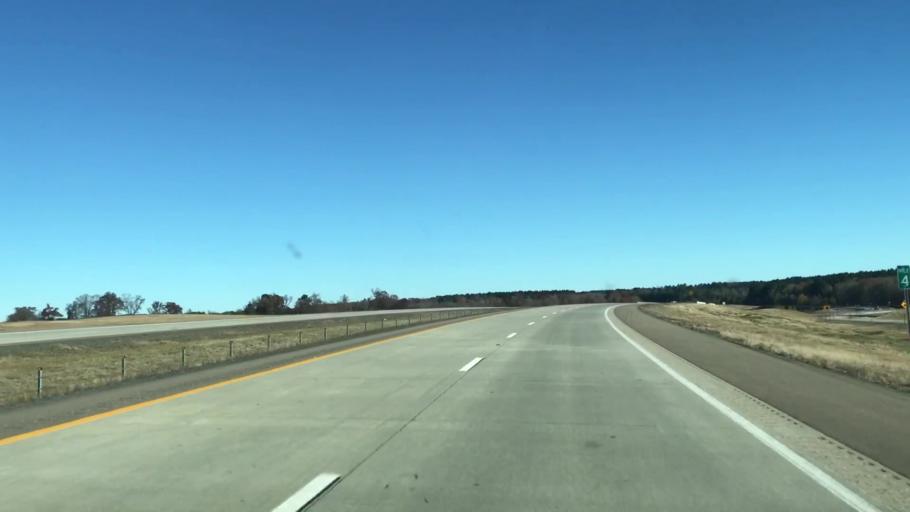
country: US
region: Louisiana
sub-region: Caddo Parish
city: Vivian
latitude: 33.0768
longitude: -93.9034
